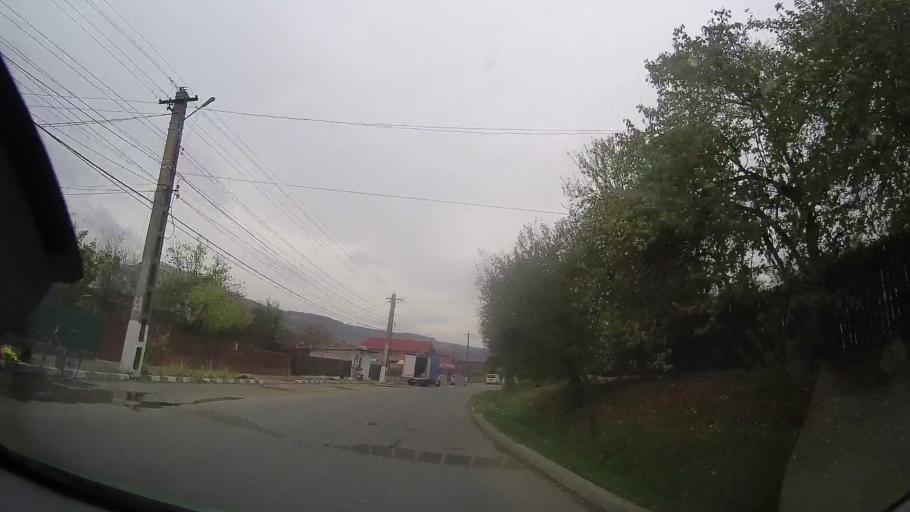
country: RO
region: Prahova
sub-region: Oras Urlati
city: Urlati
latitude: 44.9982
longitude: 26.2286
